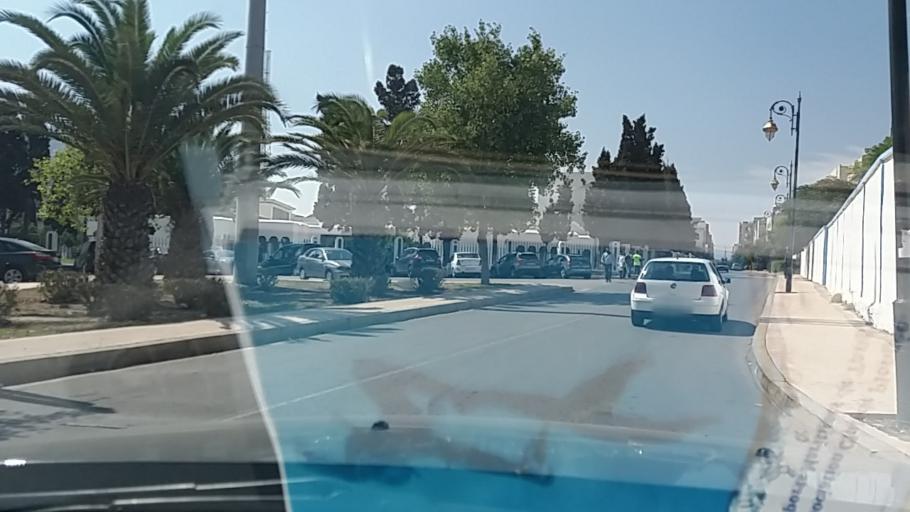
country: MA
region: Tanger-Tetouan
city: Tetouan
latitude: 35.5626
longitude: -5.3627
